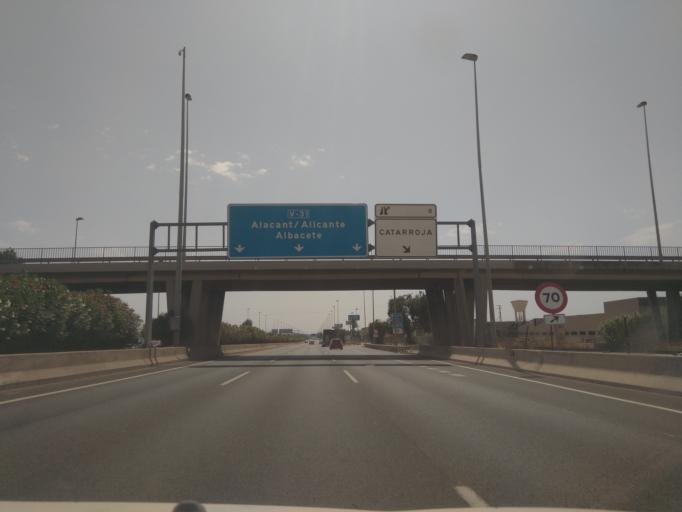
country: ES
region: Valencia
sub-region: Provincia de Valencia
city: Catarroja
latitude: 39.4017
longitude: -0.3862
